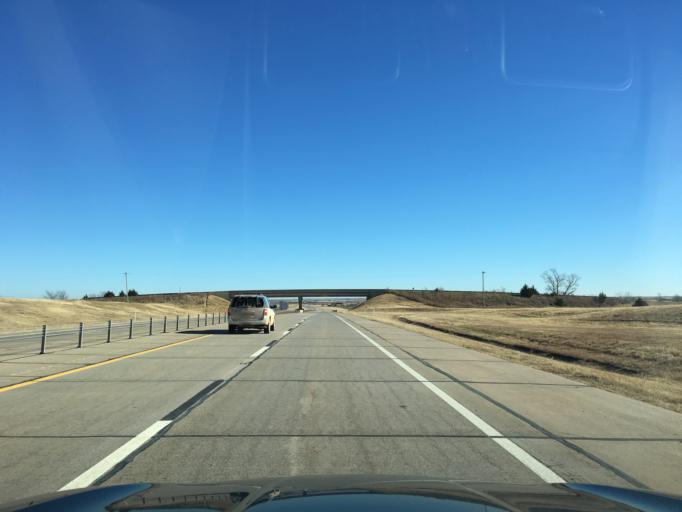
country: US
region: Oklahoma
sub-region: Noble County
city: Perry
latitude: 36.3995
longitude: -97.3032
